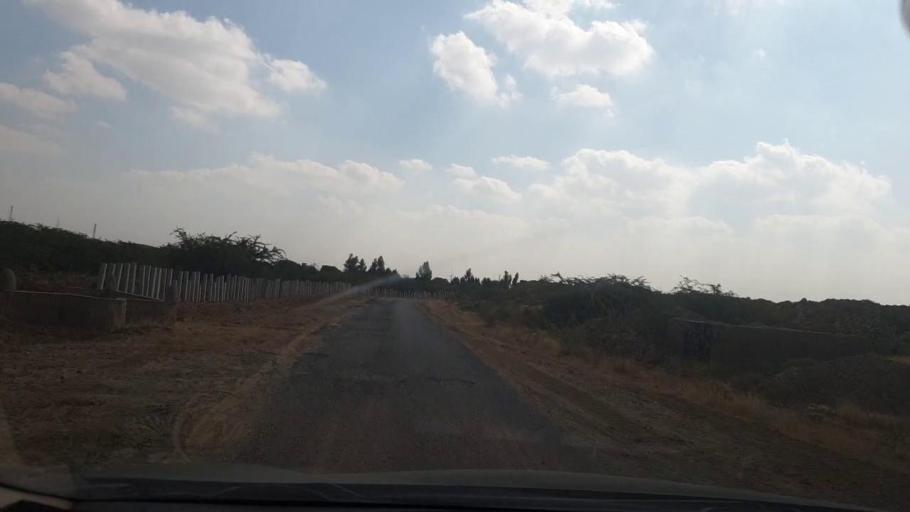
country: PK
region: Sindh
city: Malir Cantonment
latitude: 25.0233
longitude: 67.3538
